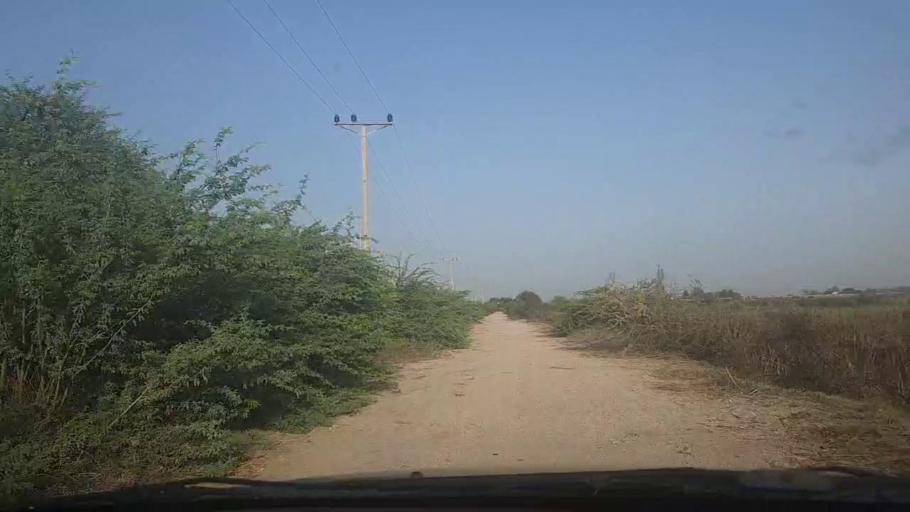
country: PK
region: Sindh
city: Keti Bandar
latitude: 24.2911
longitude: 67.6112
